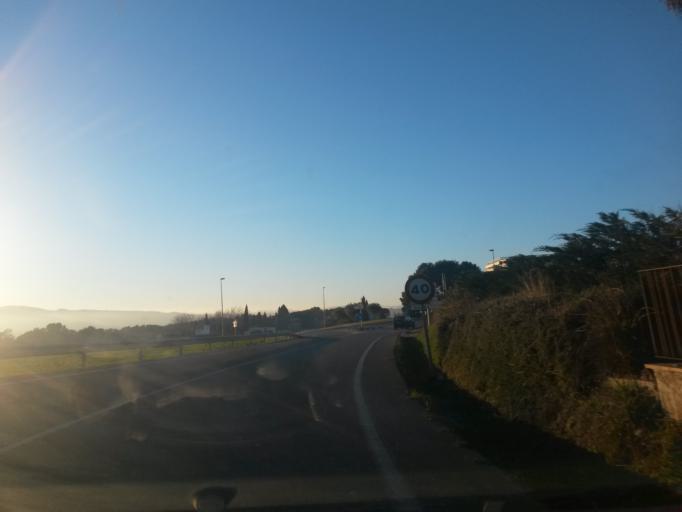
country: ES
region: Catalonia
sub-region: Provincia de Girona
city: Regencos
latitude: 41.9509
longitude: 3.1690
